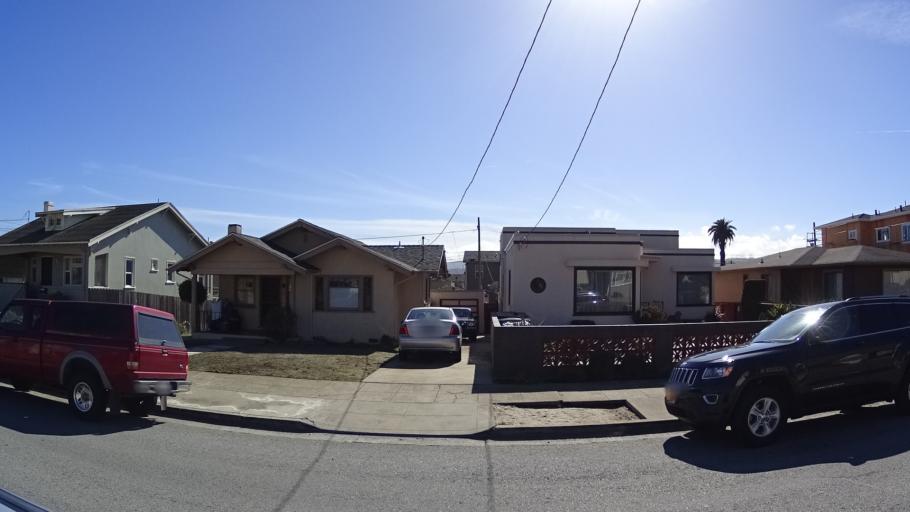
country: US
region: California
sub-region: San Mateo County
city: South San Francisco
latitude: 37.6592
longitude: -122.4233
